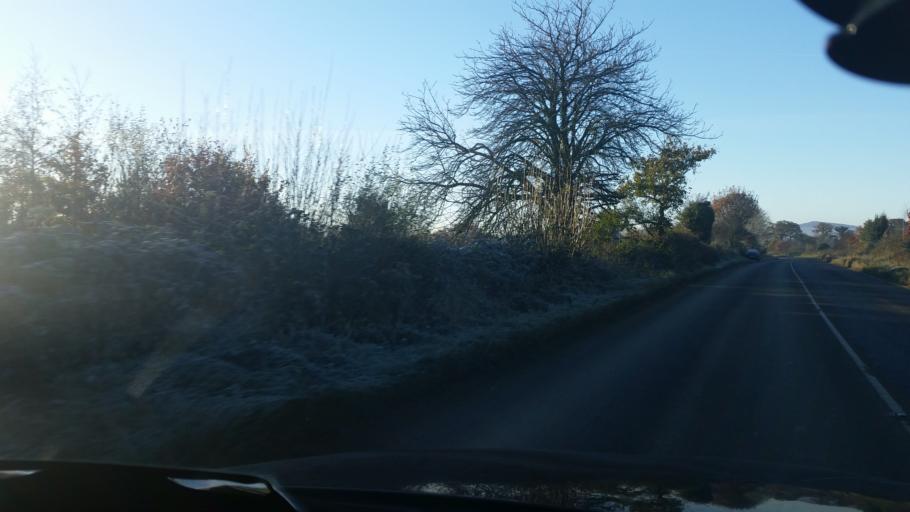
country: IE
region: Leinster
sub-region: Loch Garman
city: Gorey
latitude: 52.6387
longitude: -6.2984
